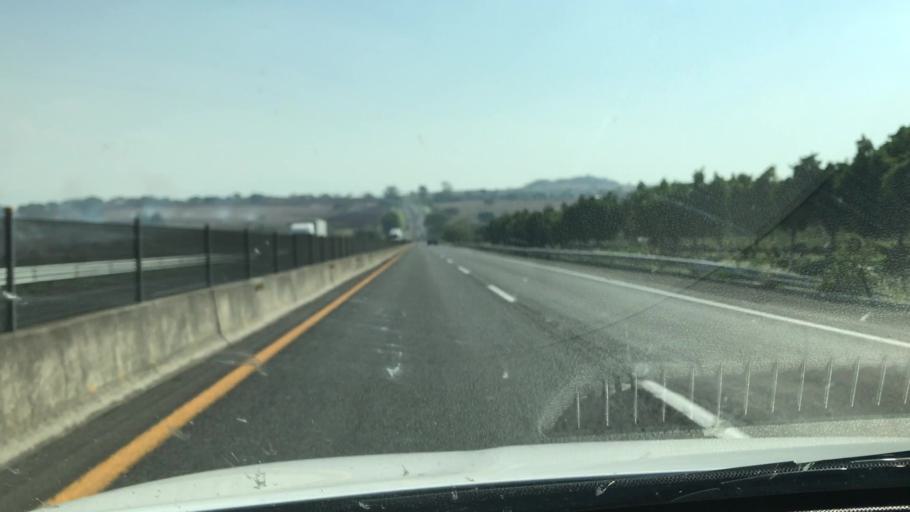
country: MX
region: Jalisco
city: Zapotlanejo
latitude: 20.6578
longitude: -103.0555
